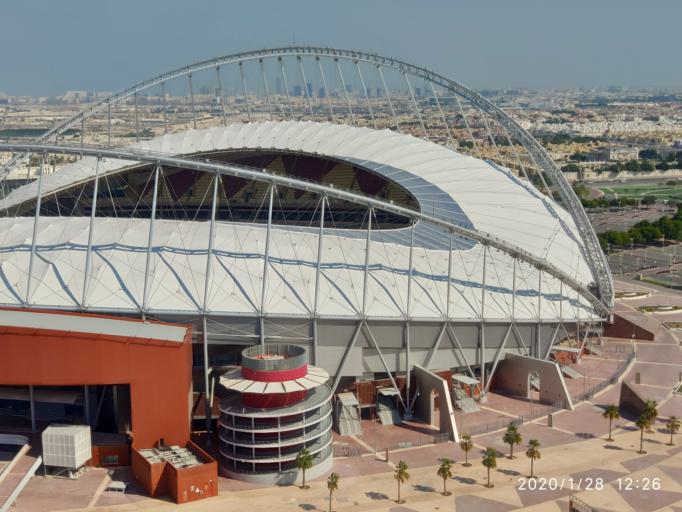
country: QA
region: Baladiyat ar Rayyan
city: Ar Rayyan
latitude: 25.2622
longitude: 51.4449
